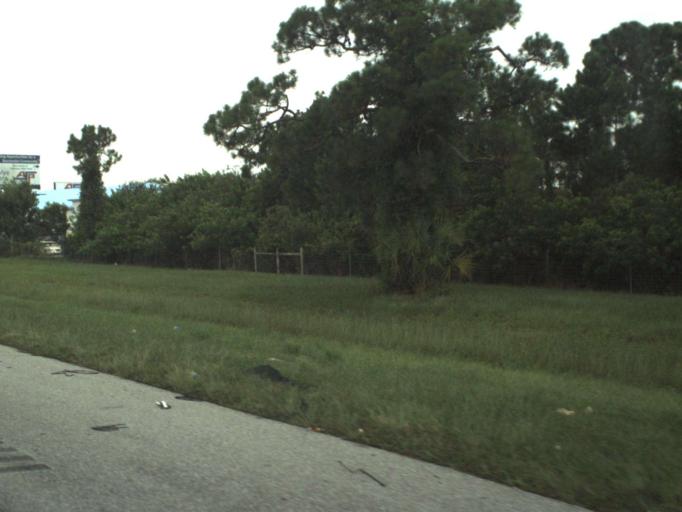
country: US
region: Florida
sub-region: Martin County
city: Palm City
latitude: 27.0961
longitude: -80.2562
